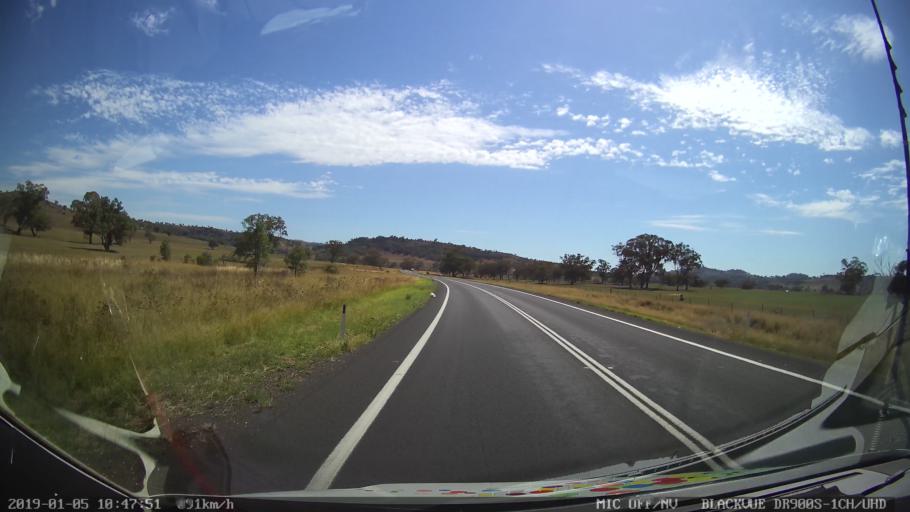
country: AU
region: New South Wales
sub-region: Warrumbungle Shire
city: Coonabarabran
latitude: -31.4416
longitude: 149.0383
